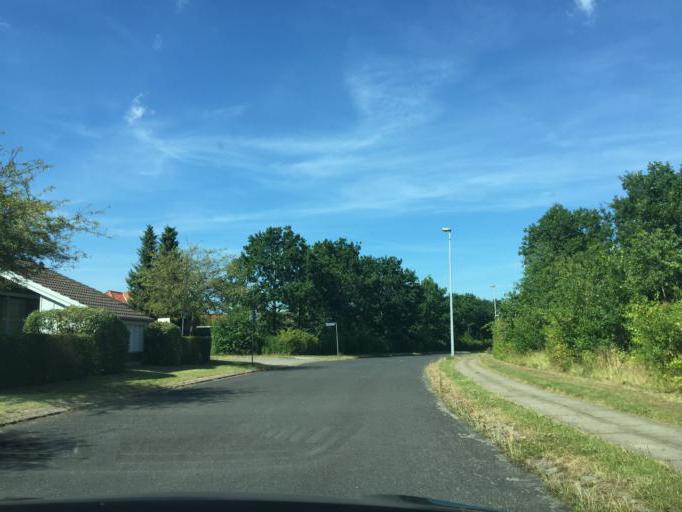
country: DK
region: South Denmark
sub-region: Odense Kommune
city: Neder Holluf
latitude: 55.3725
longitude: 10.4669
